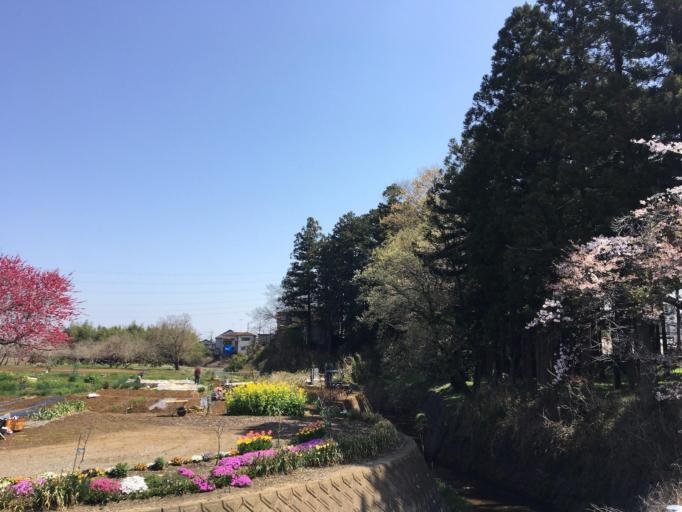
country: JP
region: Saitama
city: Sayama
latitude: 35.8957
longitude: 139.3672
